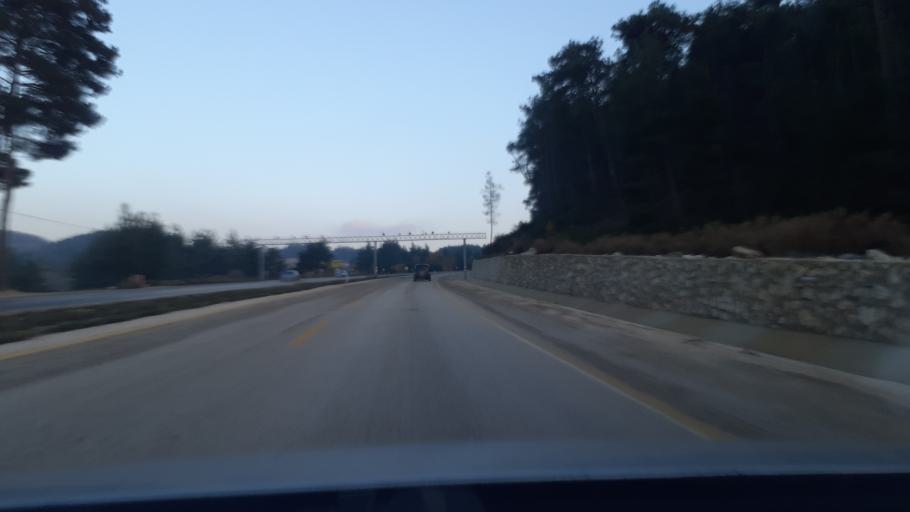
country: TR
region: Hatay
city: Yayladagi
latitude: 35.8950
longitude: 36.0807
